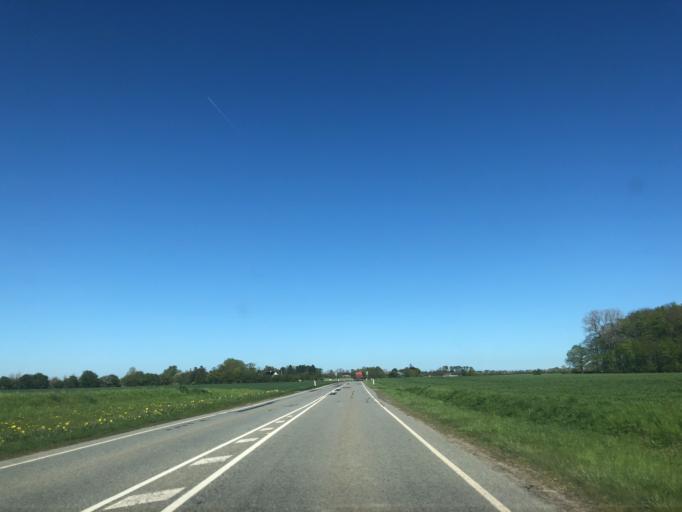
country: DK
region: Zealand
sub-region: Stevns Kommune
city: Store Heddinge
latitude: 55.2890
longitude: 12.3357
